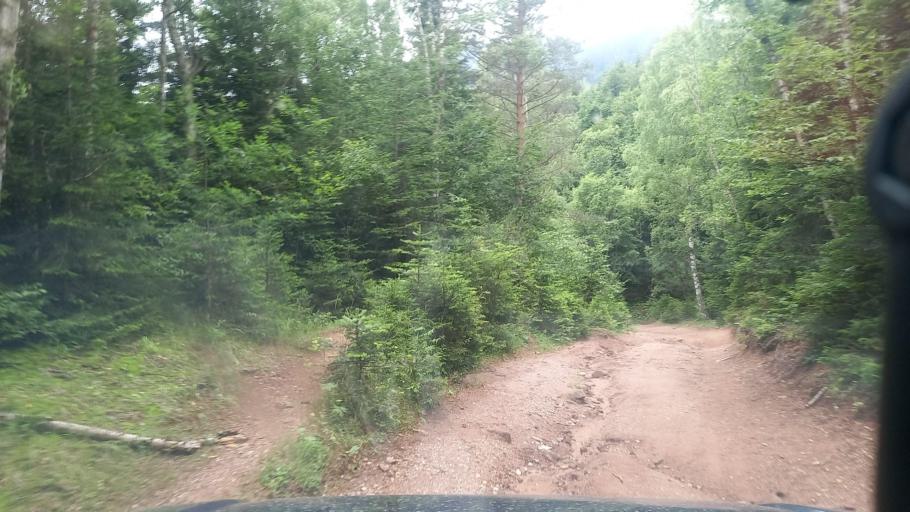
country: RU
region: Karachayevo-Cherkesiya
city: Kurdzhinovo
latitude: 43.8065
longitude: 40.8494
